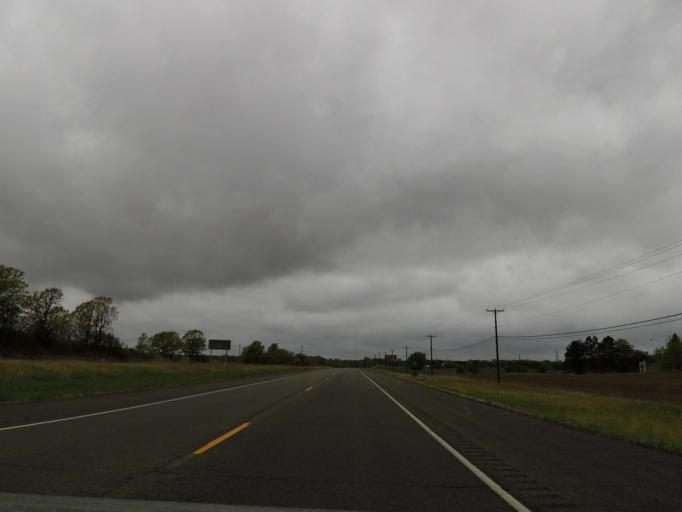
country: US
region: Minnesota
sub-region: Washington County
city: Lake Elmo
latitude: 44.9962
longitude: -92.9018
